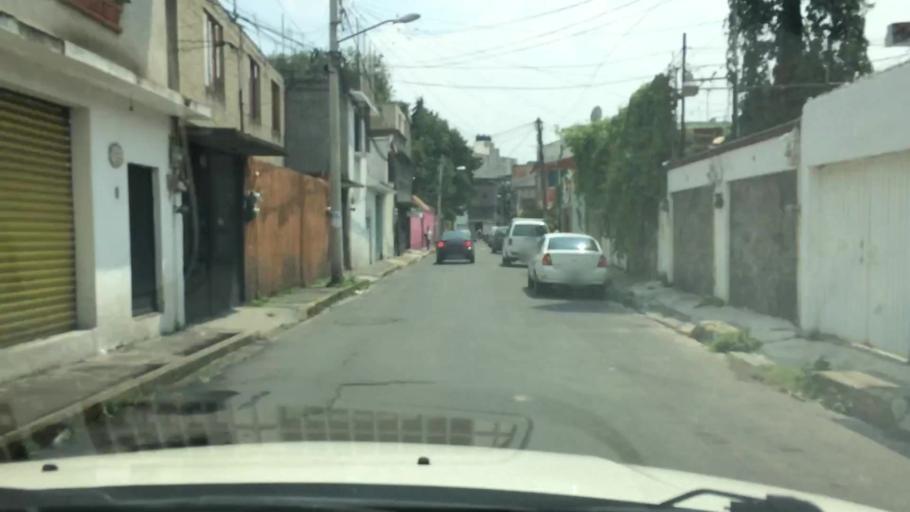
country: MX
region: Mexico City
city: Xochimilco
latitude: 19.2733
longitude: -99.1296
